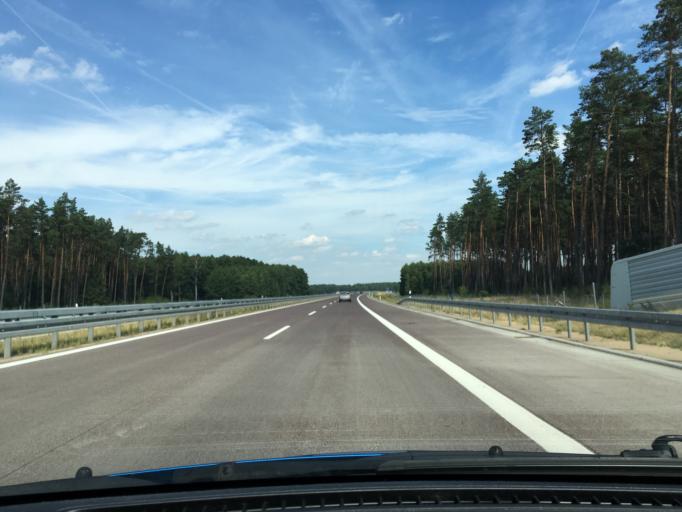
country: DE
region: Mecklenburg-Vorpommern
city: Gross Laasch
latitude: 53.3707
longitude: 11.5179
